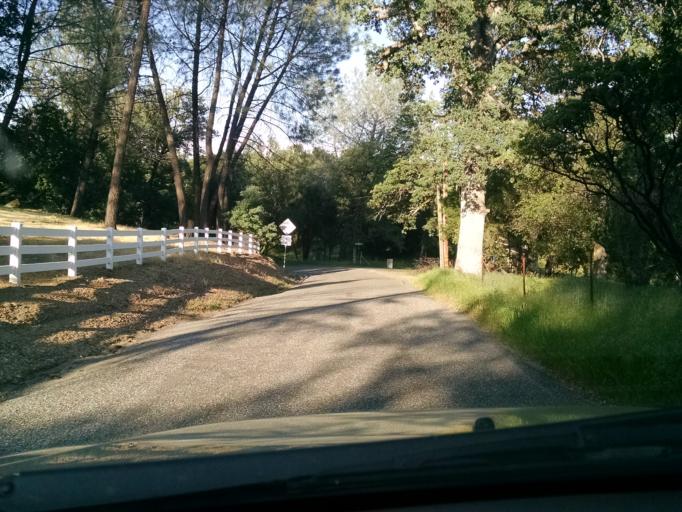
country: US
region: California
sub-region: Madera County
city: Oakhurst
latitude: 37.3095
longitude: -119.6502
